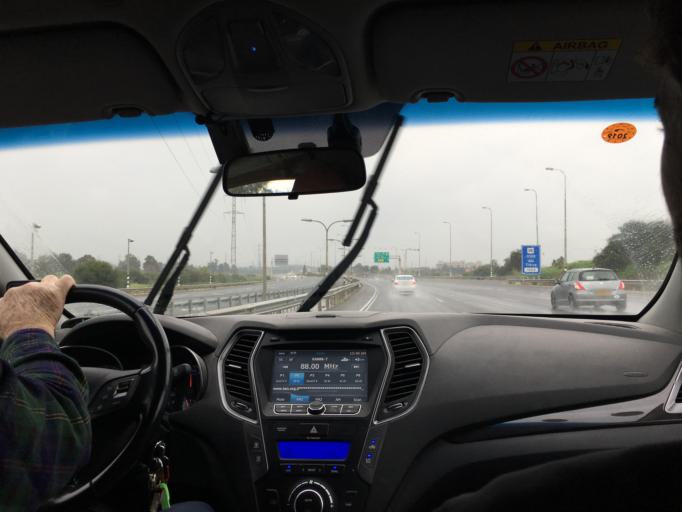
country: IL
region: Tel Aviv
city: Ramat HaSharon
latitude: 32.1220
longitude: 34.8615
